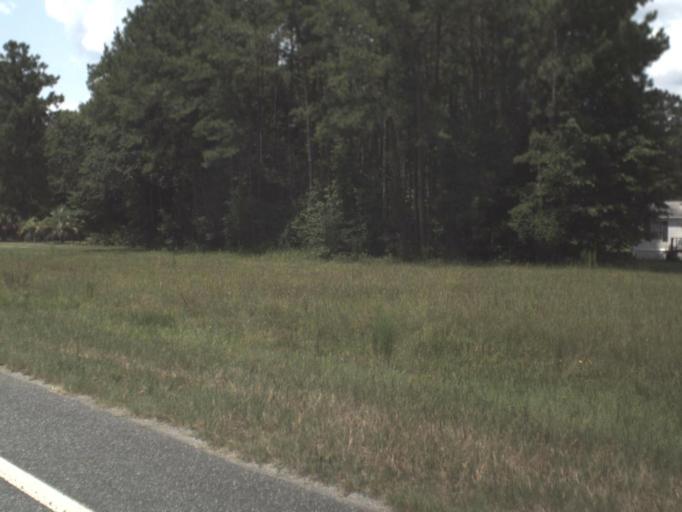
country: US
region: Florida
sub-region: Hamilton County
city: Jasper
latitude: 30.5577
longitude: -83.0670
